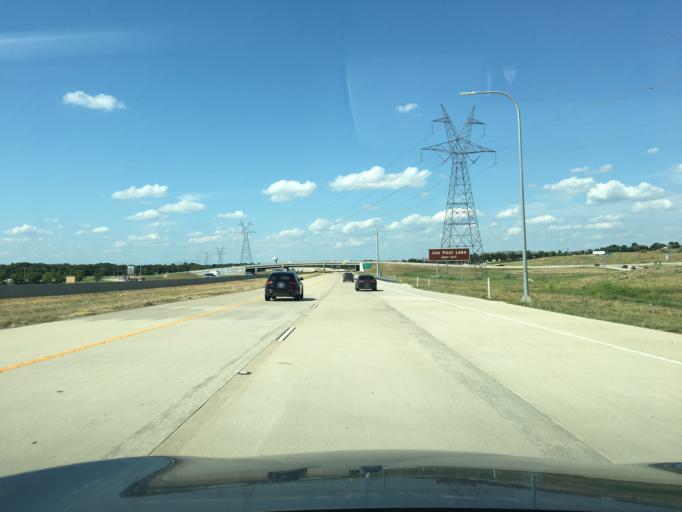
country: US
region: Texas
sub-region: Tarrant County
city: Mansfield
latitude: 32.5783
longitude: -97.0799
